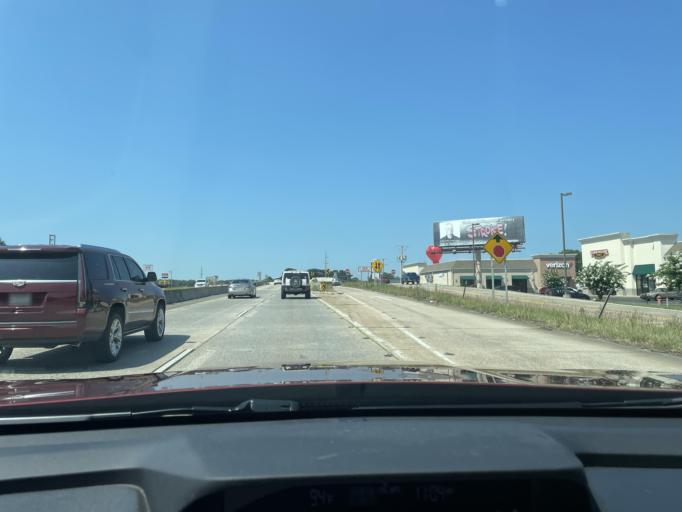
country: US
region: Arkansas
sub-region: Pulaski County
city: Jacksonville
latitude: 34.8703
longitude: -92.1249
